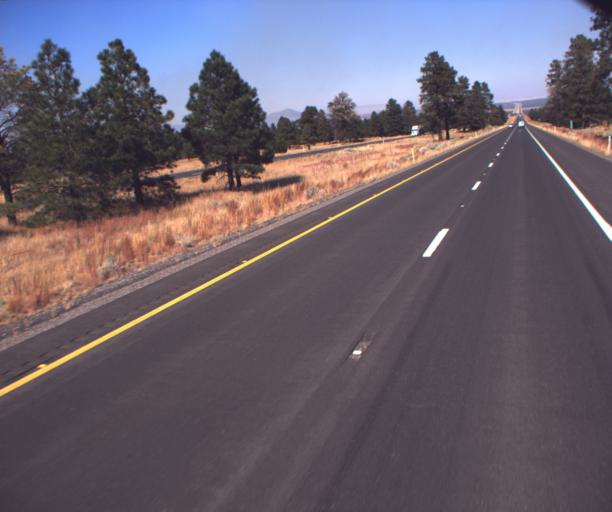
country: US
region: Arizona
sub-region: Coconino County
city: Flagstaff
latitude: 35.3927
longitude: -111.5779
